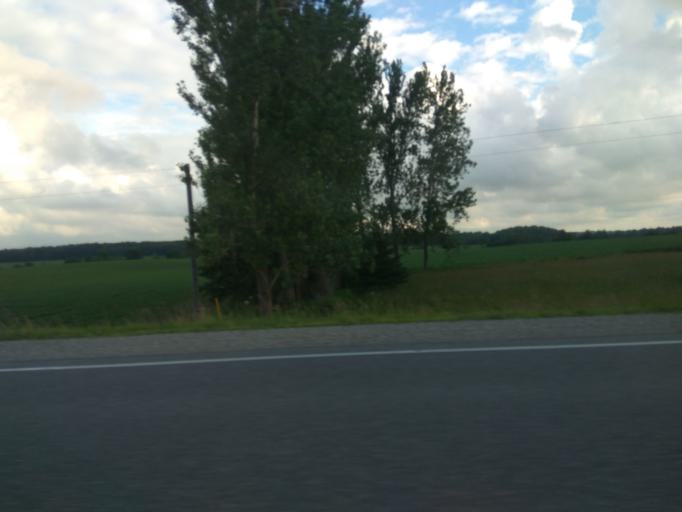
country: CA
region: Ontario
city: Stratford
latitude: 43.3693
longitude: -80.8068
